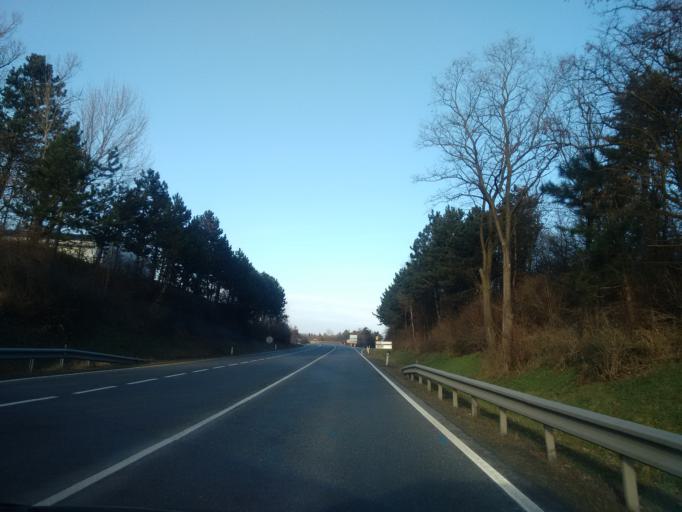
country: AT
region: Lower Austria
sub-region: Politischer Bezirk Melk
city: Melk
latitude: 48.2223
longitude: 15.3494
